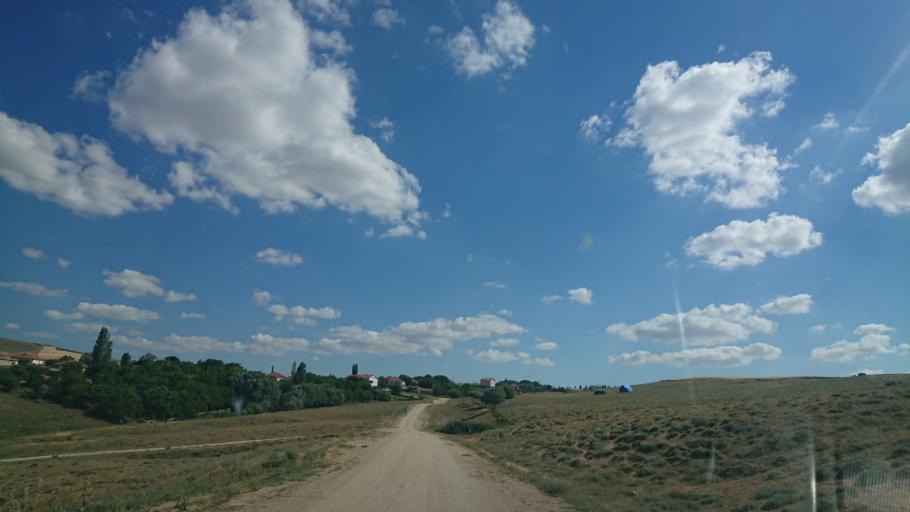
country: TR
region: Aksaray
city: Agacoren
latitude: 38.9081
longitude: 33.8564
